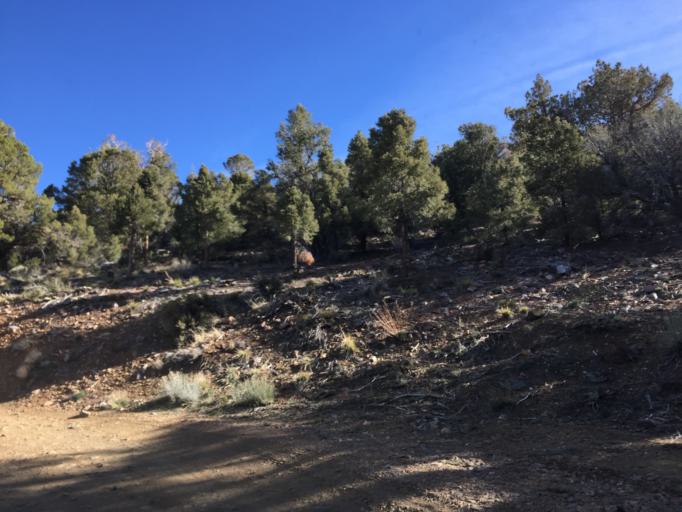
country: US
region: California
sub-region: San Bernardino County
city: Big Bear City
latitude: 34.2102
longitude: -116.7294
